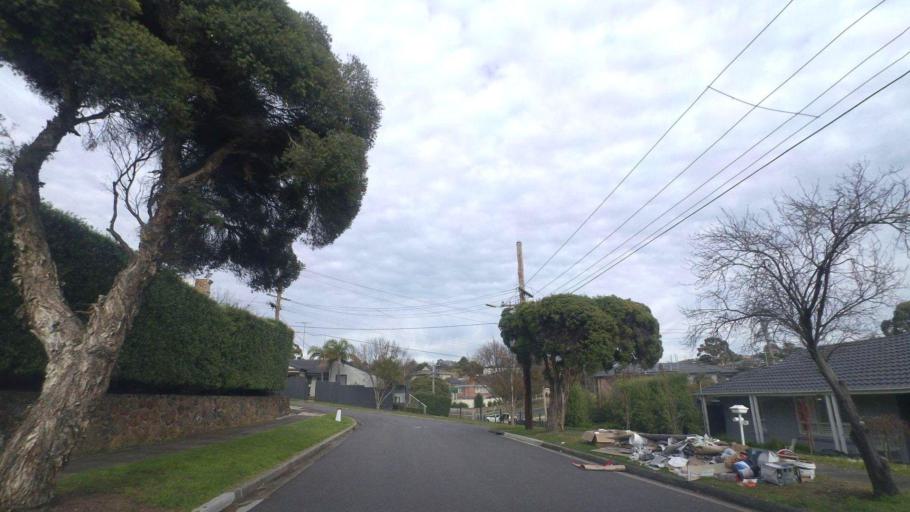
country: AU
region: Victoria
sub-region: Manningham
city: Templestowe Lower
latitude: -37.7623
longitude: 145.1126
